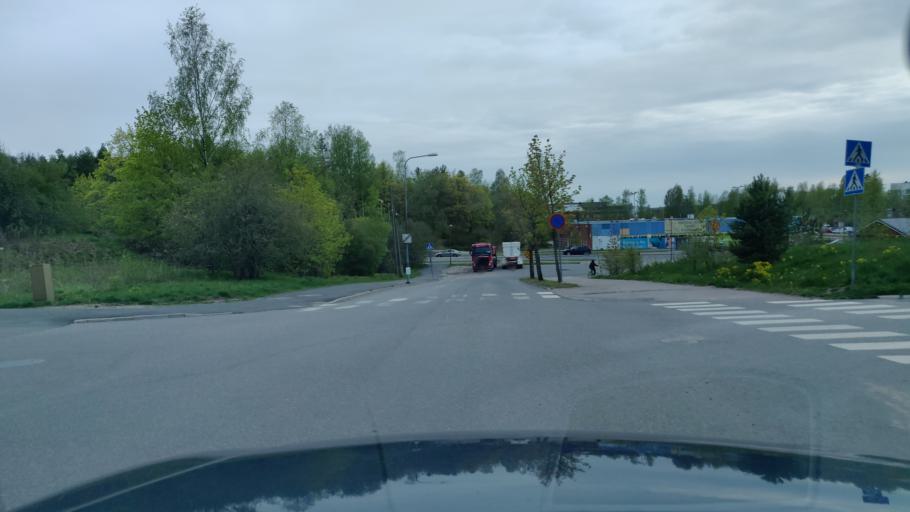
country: FI
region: Uusimaa
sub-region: Helsinki
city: Nurmijaervi
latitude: 60.3821
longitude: 24.7512
